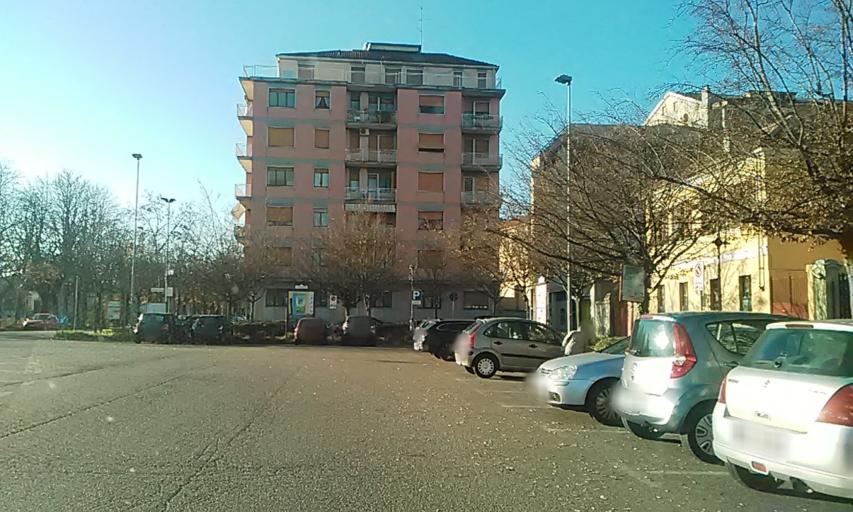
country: IT
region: Piedmont
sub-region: Provincia di Alessandria
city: Casale Monferrato
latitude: 45.1342
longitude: 8.4591
